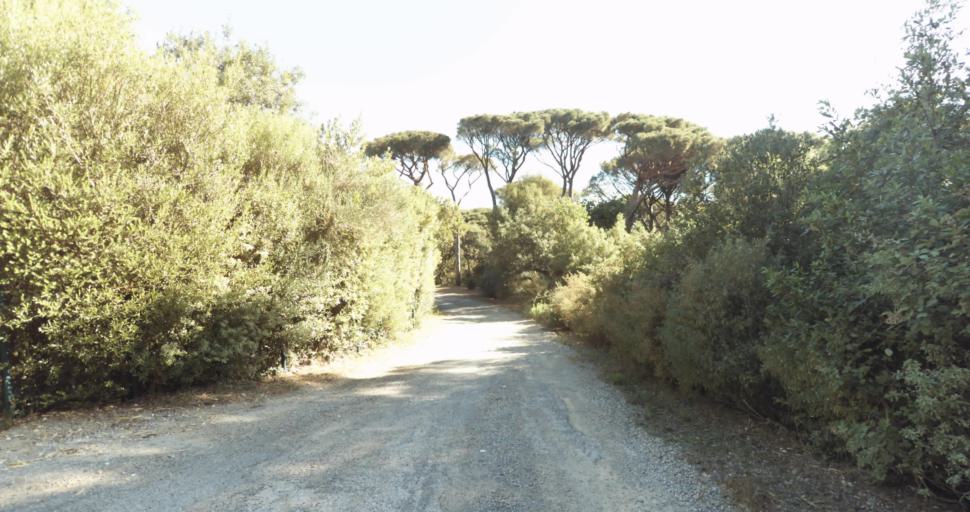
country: FR
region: Provence-Alpes-Cote d'Azur
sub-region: Departement du Var
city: Saint-Tropez
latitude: 43.2579
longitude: 6.6209
